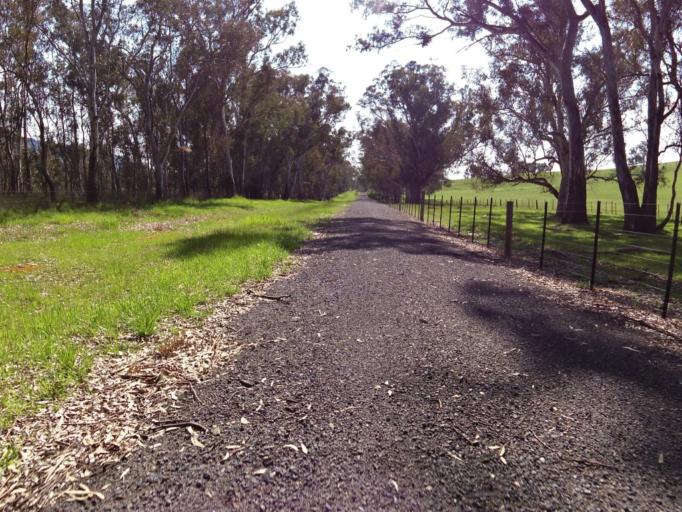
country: AU
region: Victoria
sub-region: Murrindindi
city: Alexandra
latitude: -37.1398
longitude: 145.5902
